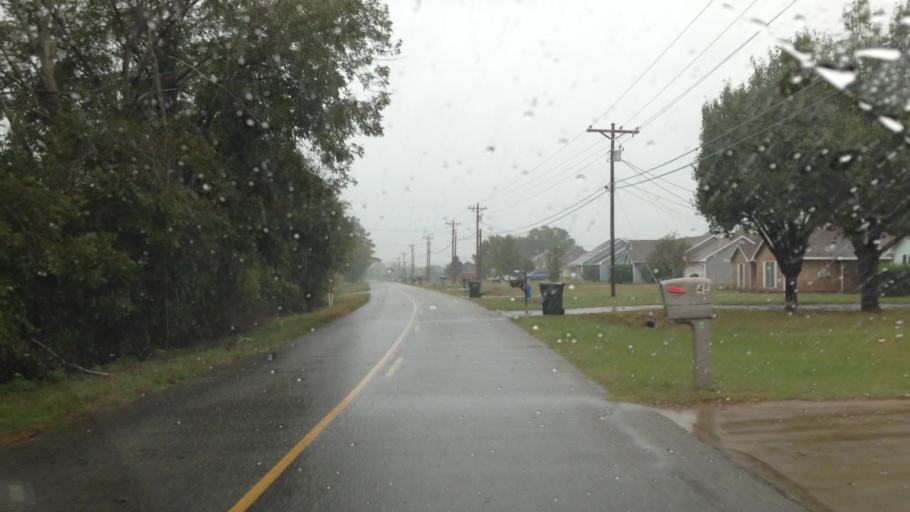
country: US
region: Georgia
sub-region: Muscogee County
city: Columbus
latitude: 32.2636
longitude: -84.9790
